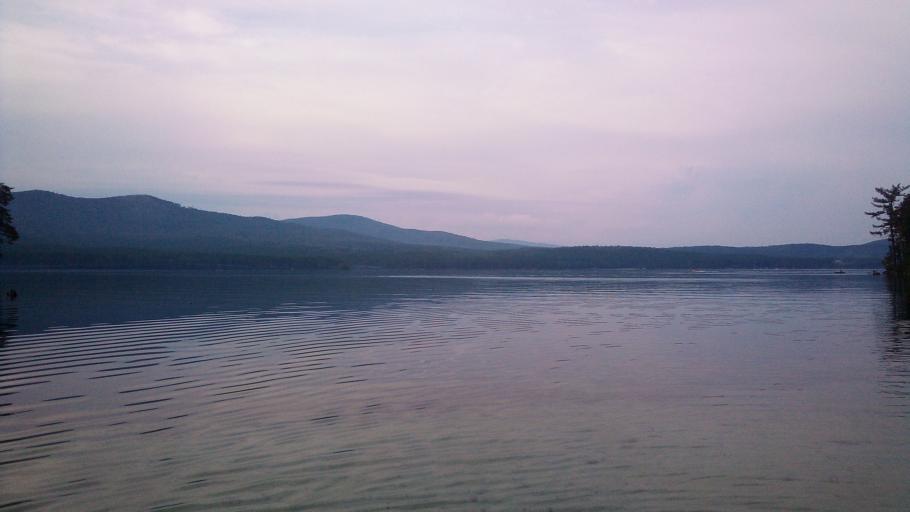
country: RU
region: Chelyabinsk
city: Turgoyak
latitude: 55.1603
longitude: 60.0286
